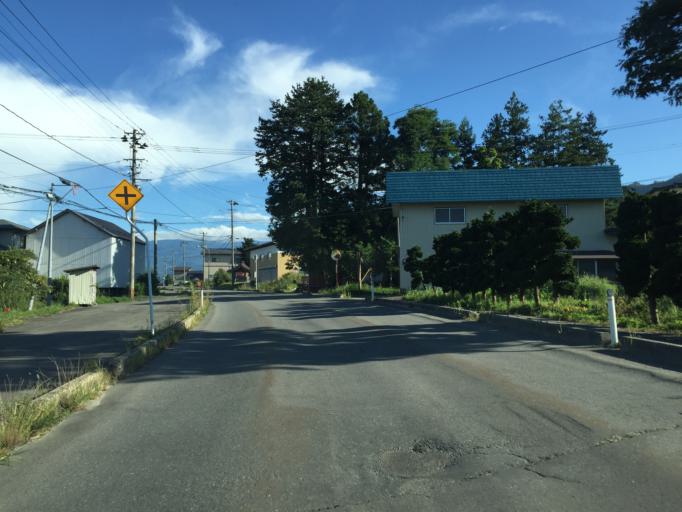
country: JP
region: Yamagata
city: Yonezawa
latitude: 37.9033
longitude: 140.0839
